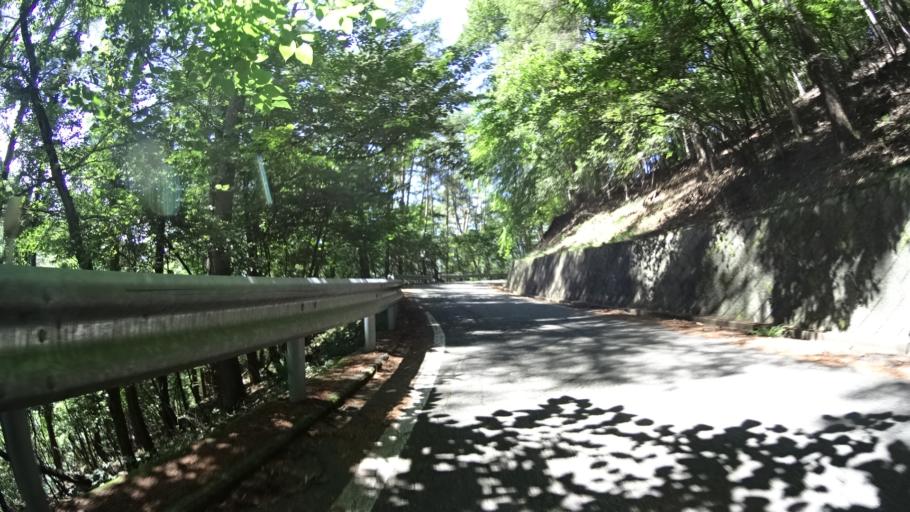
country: JP
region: Yamanashi
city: Enzan
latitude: 35.7414
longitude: 138.8165
